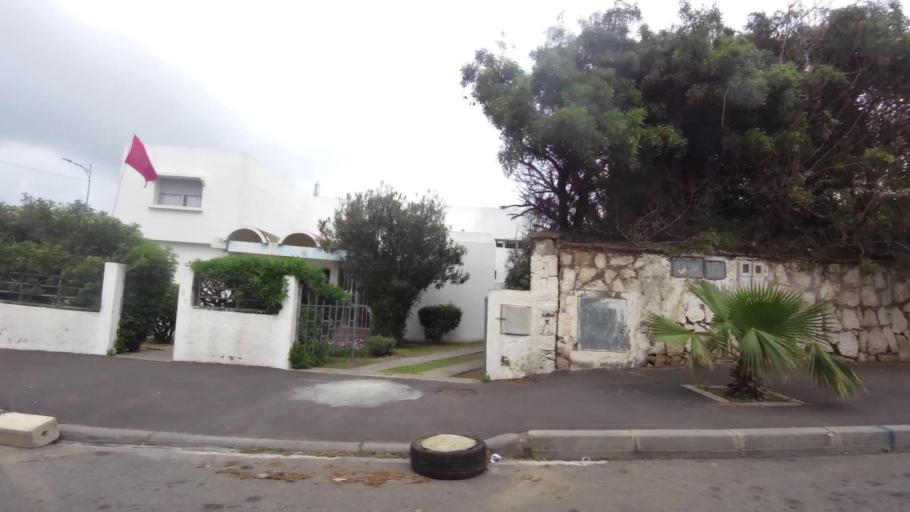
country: MA
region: Grand Casablanca
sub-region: Casablanca
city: Casablanca
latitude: 33.6049
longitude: -7.6566
